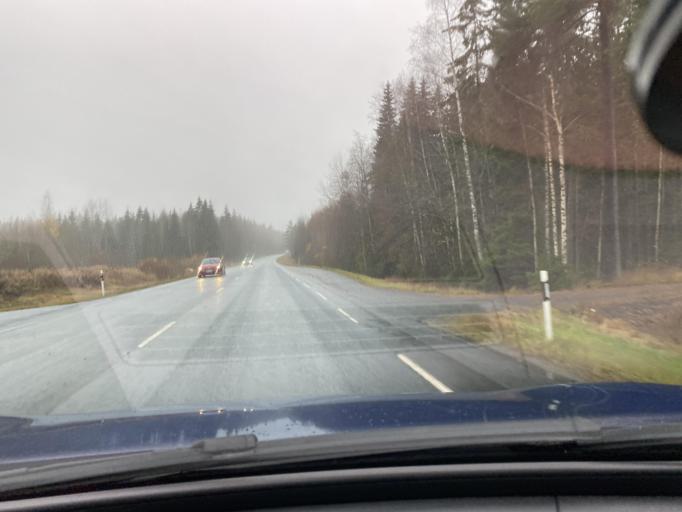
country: FI
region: Haeme
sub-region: Forssa
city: Jokioinen
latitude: 60.7940
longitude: 23.5041
